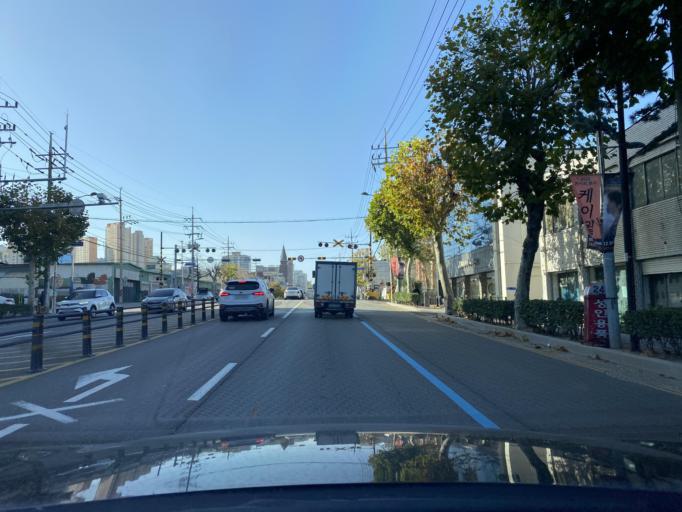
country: KR
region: Incheon
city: Incheon
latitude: 37.4870
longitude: 126.7353
